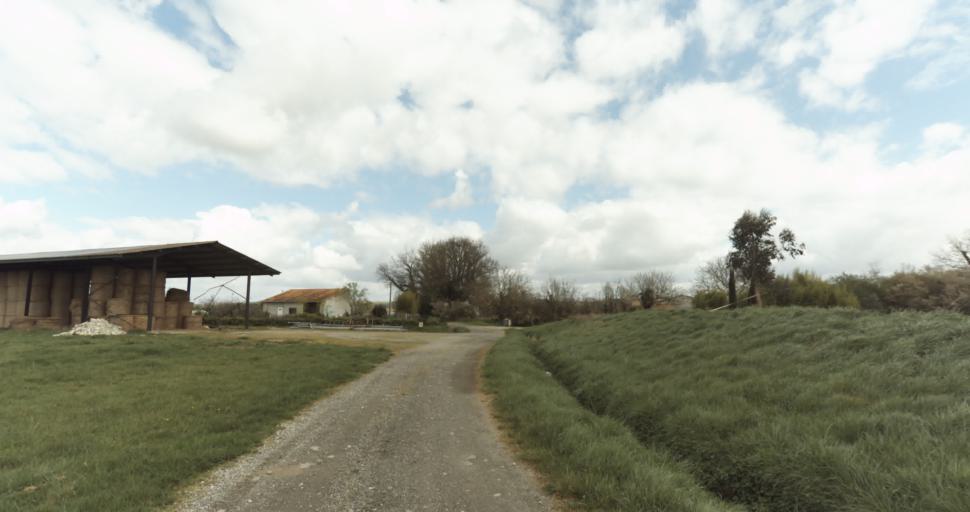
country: FR
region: Midi-Pyrenees
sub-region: Departement de la Haute-Garonne
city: Auterive
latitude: 43.3388
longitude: 1.4695
